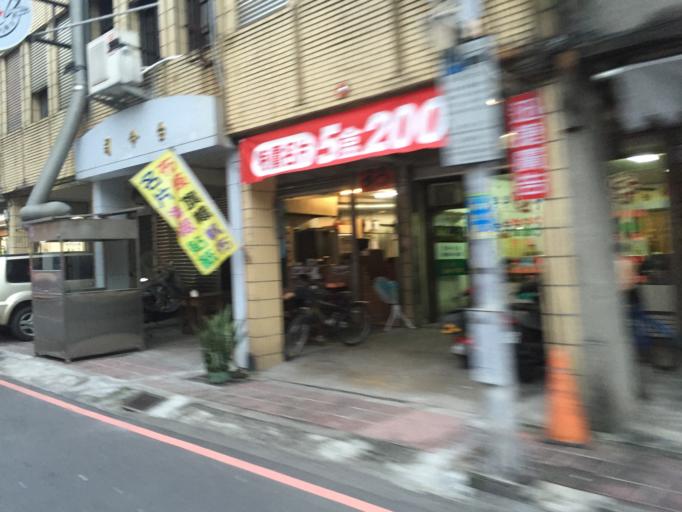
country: TW
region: Taiwan
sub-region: Yilan
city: Yilan
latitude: 24.7635
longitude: 121.7544
